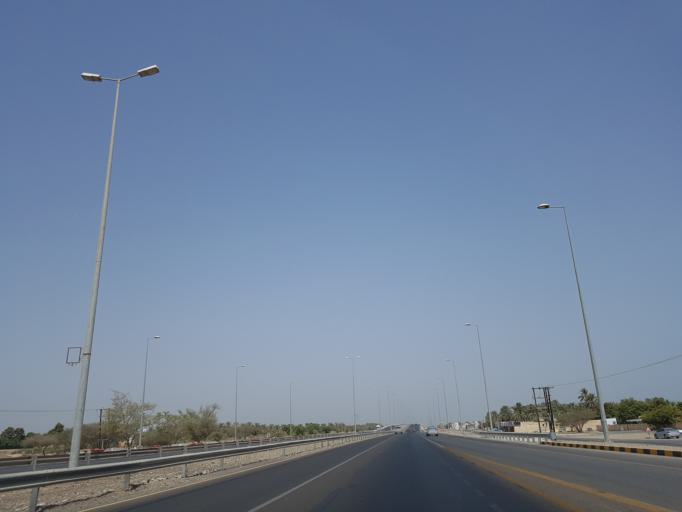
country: OM
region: Al Batinah
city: Saham
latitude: 24.0695
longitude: 56.9519
